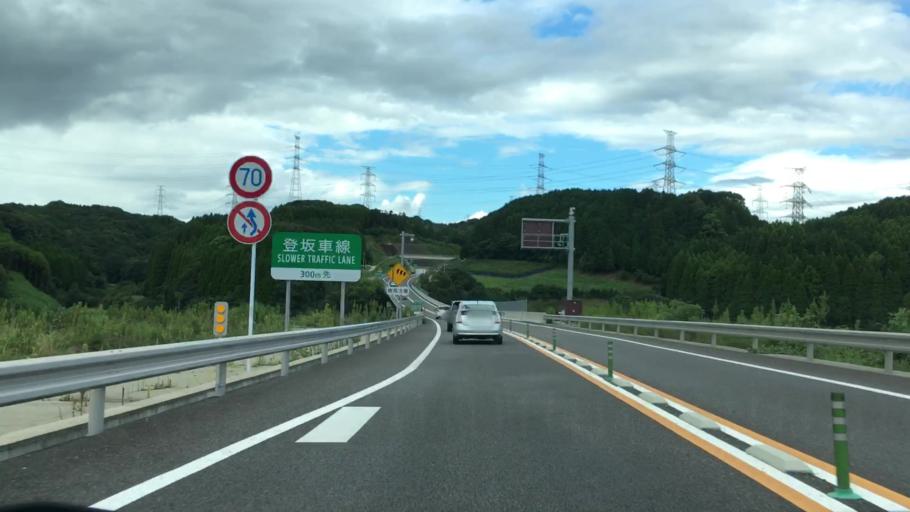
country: JP
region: Saga Prefecture
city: Imaricho-ko
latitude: 33.3468
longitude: 129.9247
